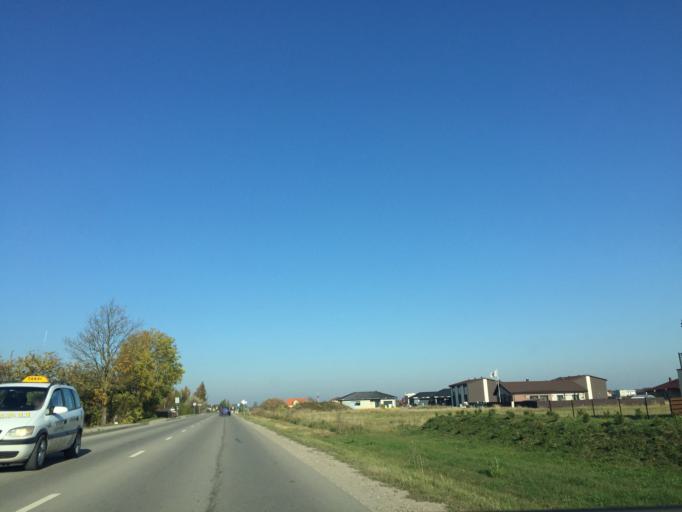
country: LT
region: Klaipedos apskritis
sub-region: Klaipeda
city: Klaipeda
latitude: 55.7408
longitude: 21.1925
